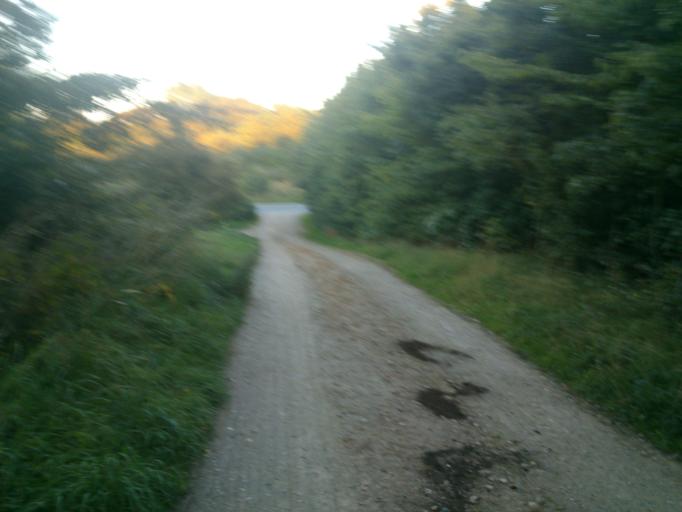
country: DK
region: South Denmark
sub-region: Fredericia Kommune
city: Fredericia
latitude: 55.5716
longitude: 9.7079
